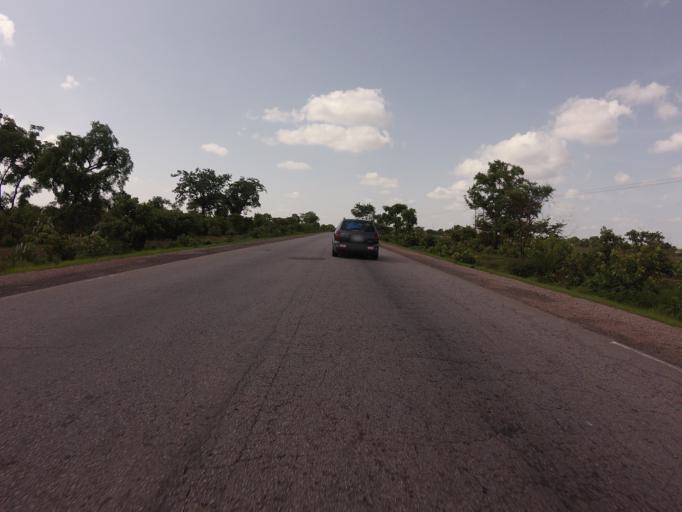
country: GH
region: Northern
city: Savelugu
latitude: 9.9396
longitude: -0.8411
